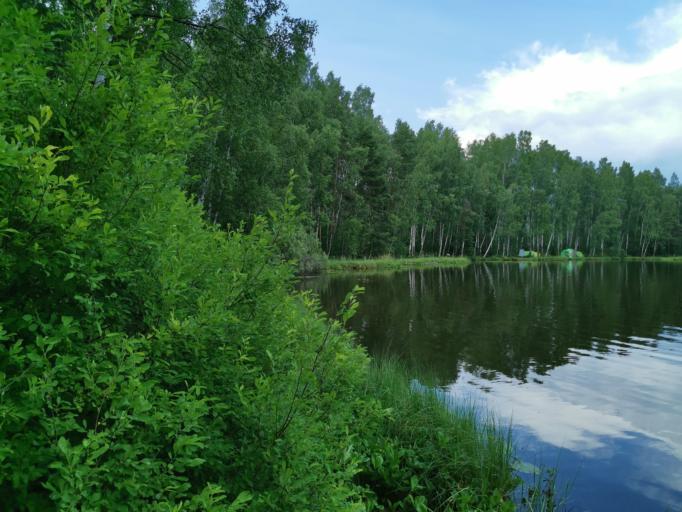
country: RU
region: St.-Petersburg
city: Pargolovo
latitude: 60.1137
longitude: 30.2969
